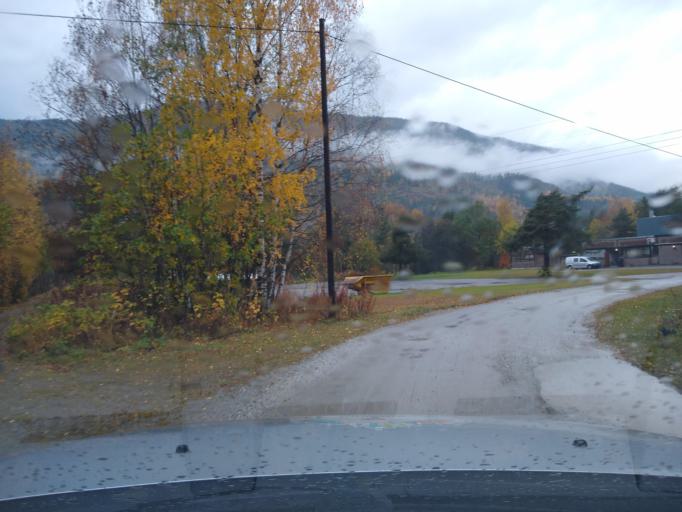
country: NO
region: Oppland
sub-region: Ringebu
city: Ringebu
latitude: 61.5239
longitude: 10.1374
